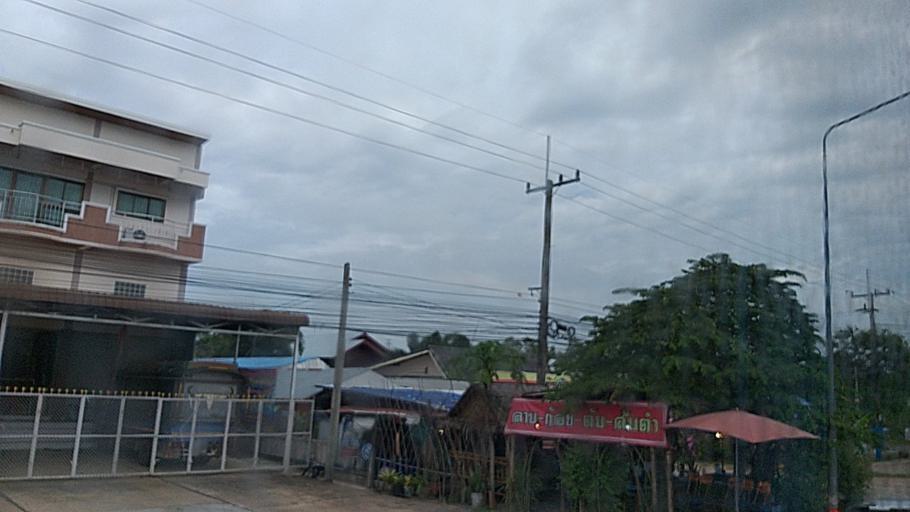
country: TH
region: Maha Sarakham
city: Maha Sarakham
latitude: 16.1458
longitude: 103.4122
